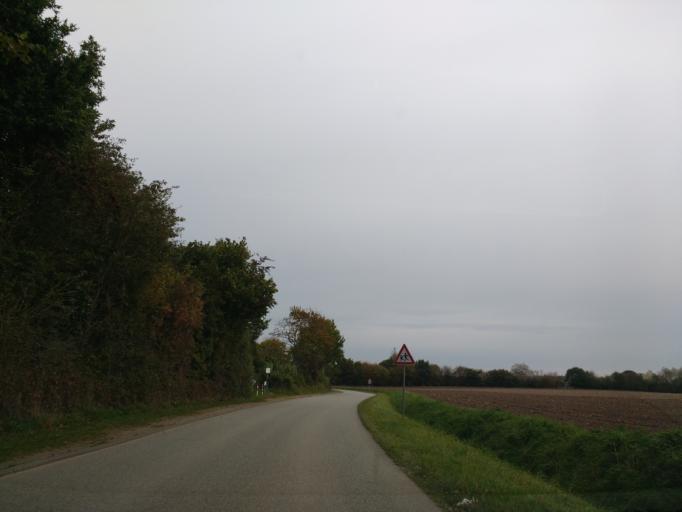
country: DE
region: Schleswig-Holstein
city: Grube
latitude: 54.2013
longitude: 11.0206
